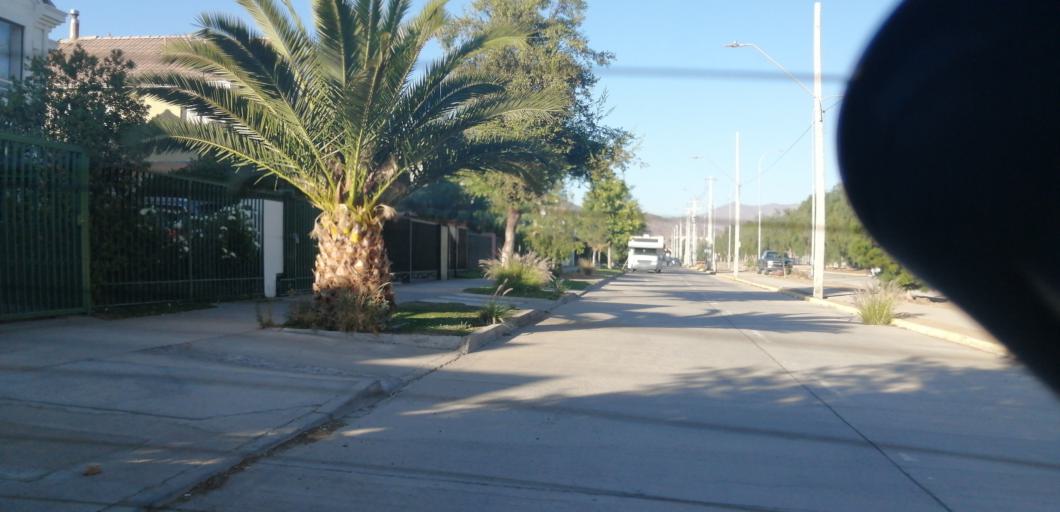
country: CL
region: Santiago Metropolitan
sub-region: Provincia de Santiago
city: Lo Prado
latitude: -33.4460
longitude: -70.8406
